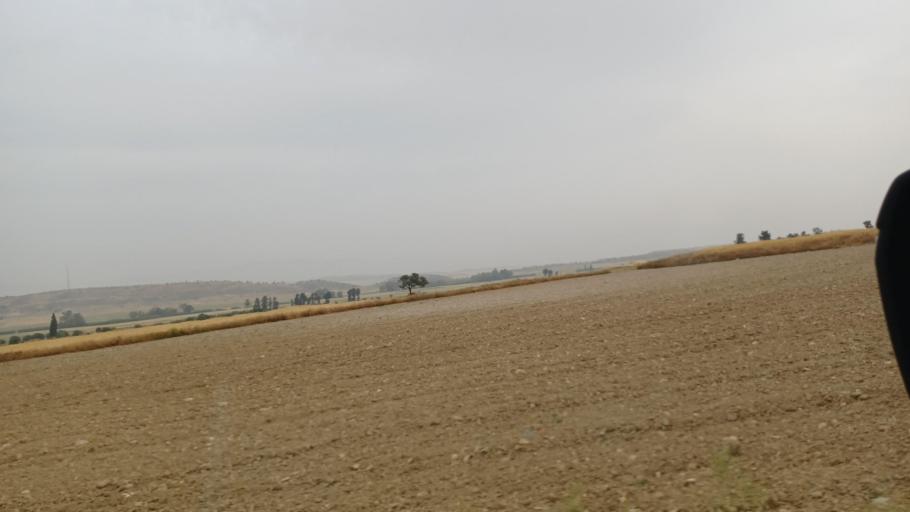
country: CY
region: Lefkosia
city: Mammari
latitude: 35.1782
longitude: 33.1957
